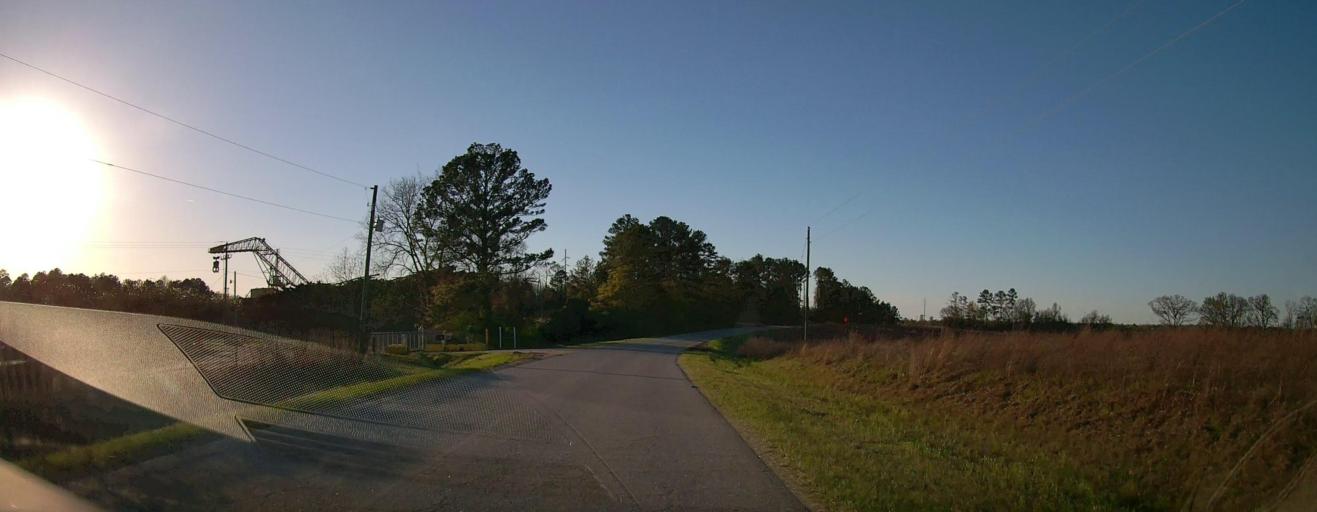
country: US
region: Georgia
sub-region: Wilkinson County
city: Gordon
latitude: 32.8904
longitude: -83.2996
